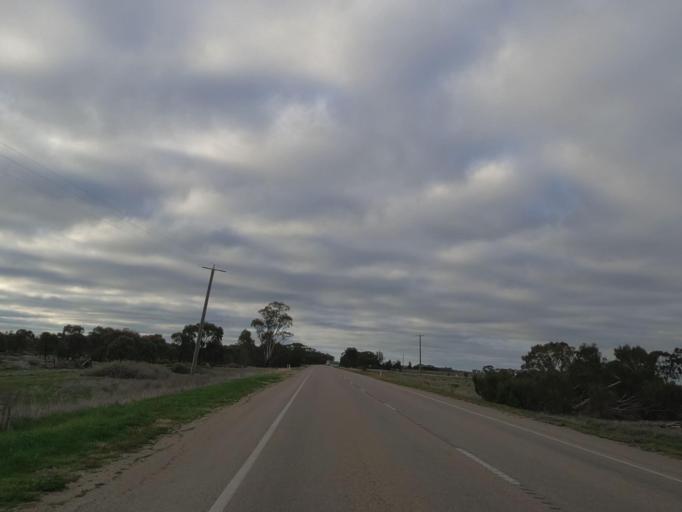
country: AU
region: Victoria
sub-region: Swan Hill
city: Swan Hill
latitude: -35.8231
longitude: 143.9488
